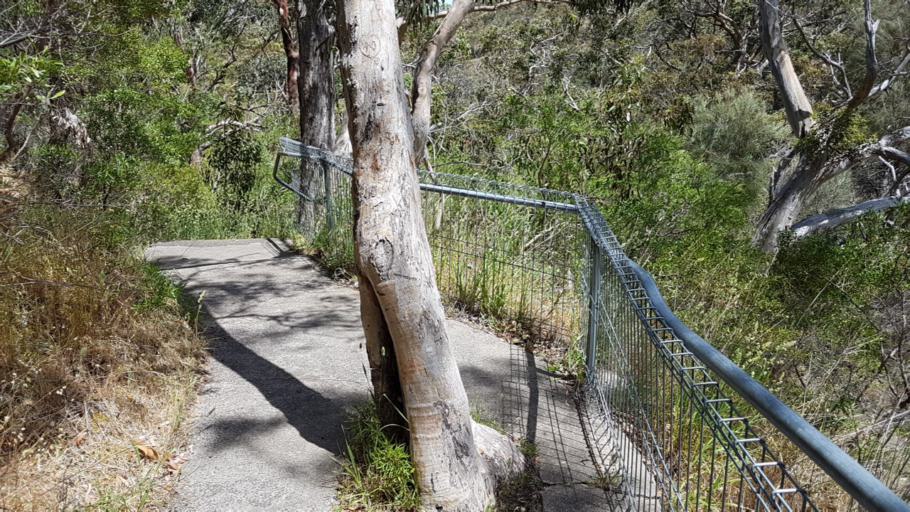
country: AU
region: South Australia
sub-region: Alexandrina
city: Mount Compass
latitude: -35.4430
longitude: 138.5842
